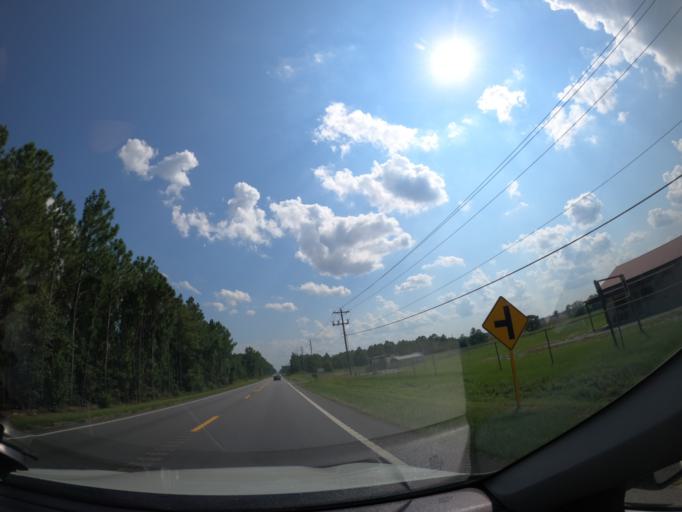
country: US
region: South Carolina
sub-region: Lexington County
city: Gaston
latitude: 33.8002
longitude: -81.2290
